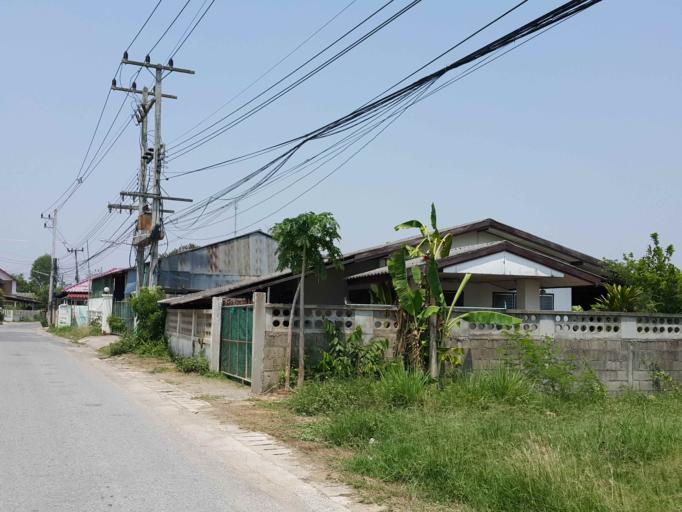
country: TH
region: Chiang Mai
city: San Kamphaeng
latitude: 18.7918
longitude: 99.0849
